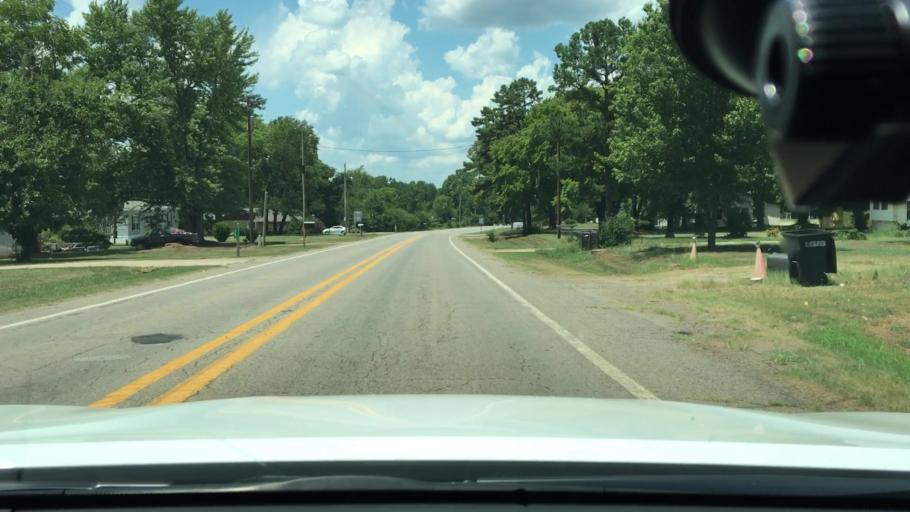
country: US
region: Arkansas
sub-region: Logan County
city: Booneville
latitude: 35.1499
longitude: -93.8135
